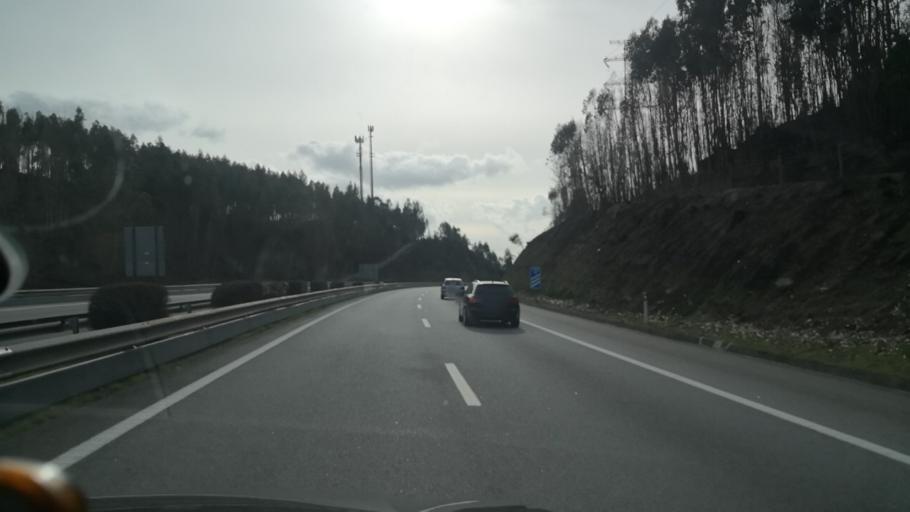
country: PT
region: Porto
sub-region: Paredes
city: Baltar
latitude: 41.1750
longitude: -8.3789
